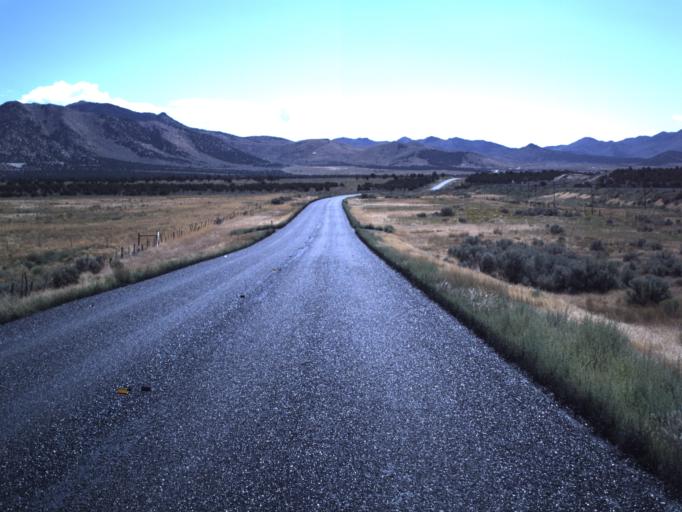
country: US
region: Utah
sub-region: Utah County
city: Genola
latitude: 39.9405
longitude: -112.1876
